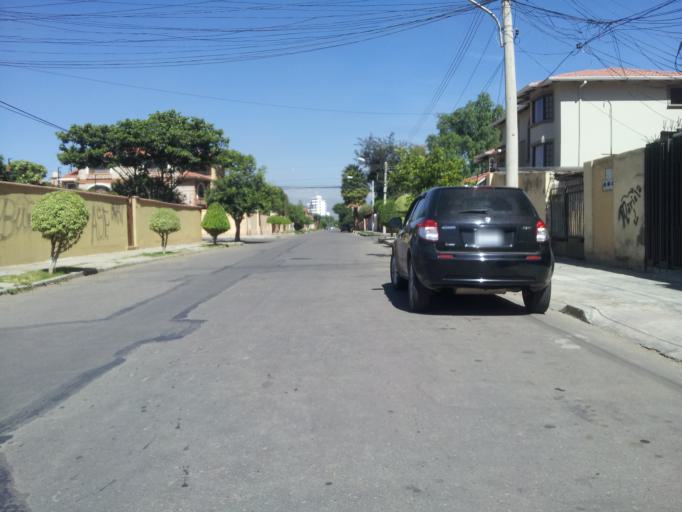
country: BO
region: Cochabamba
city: Cochabamba
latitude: -17.3819
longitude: -66.1708
